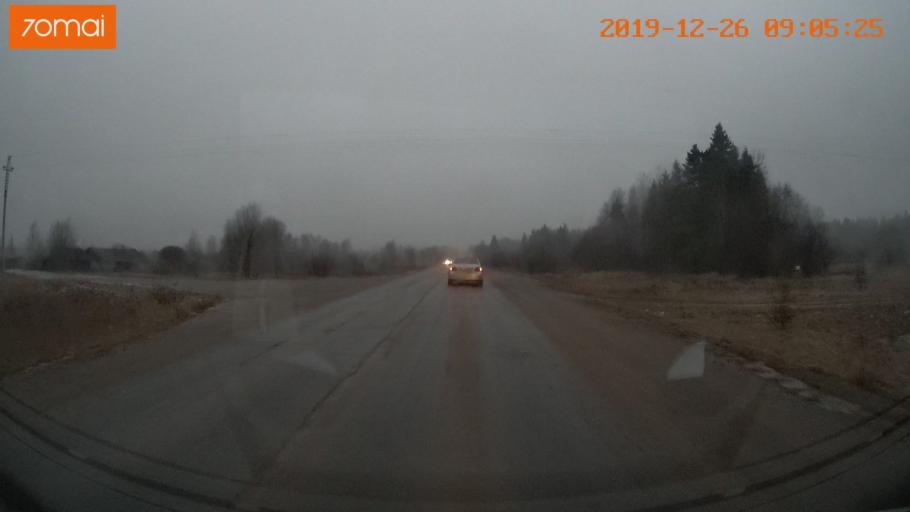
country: RU
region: Vologda
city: Gryazovets
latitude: 58.8253
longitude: 40.2582
